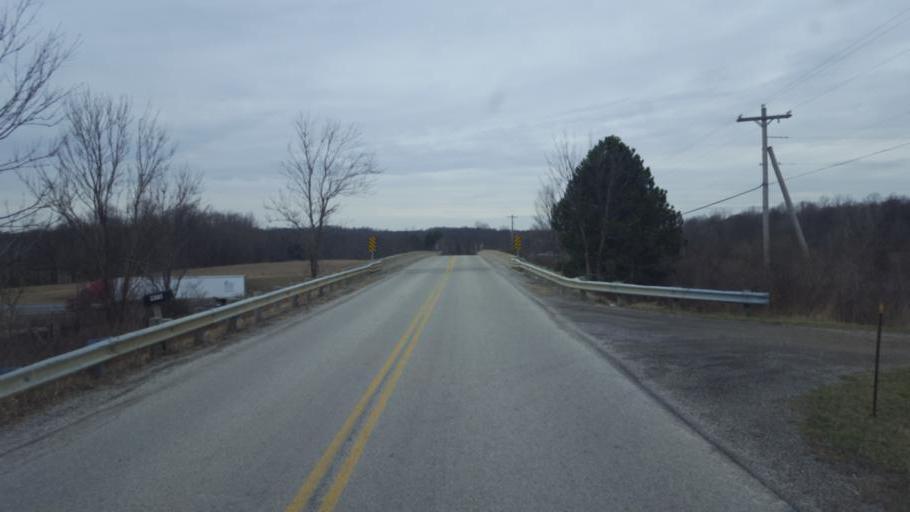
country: US
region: Ohio
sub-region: Richland County
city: Mansfield
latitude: 40.7136
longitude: -82.4851
